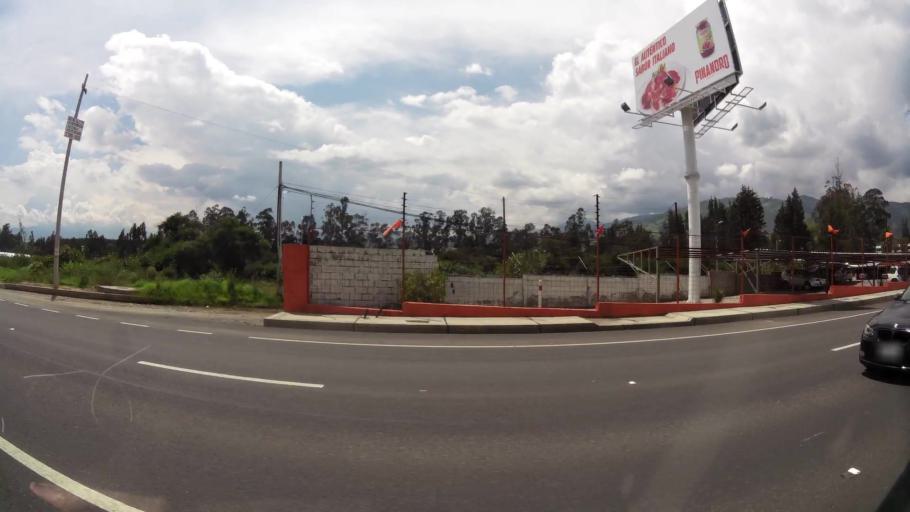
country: EC
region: Pichincha
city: Sangolqui
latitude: -0.1991
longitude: -78.3371
